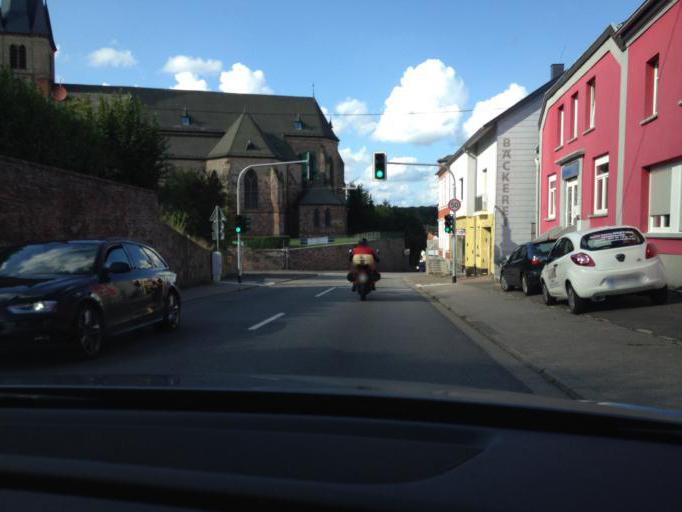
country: DE
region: Saarland
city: Schmelz
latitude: 49.4852
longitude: 6.8398
